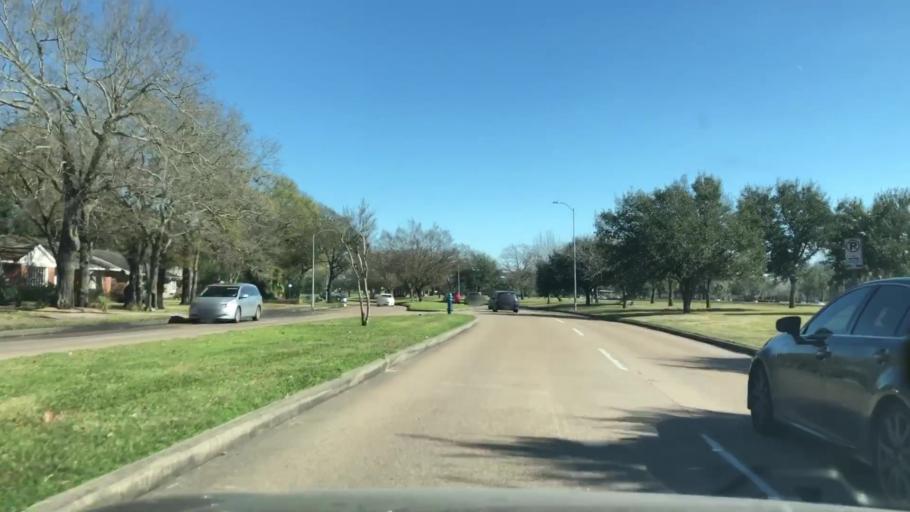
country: US
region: Texas
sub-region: Harris County
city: Bellaire
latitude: 29.6800
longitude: -95.4642
